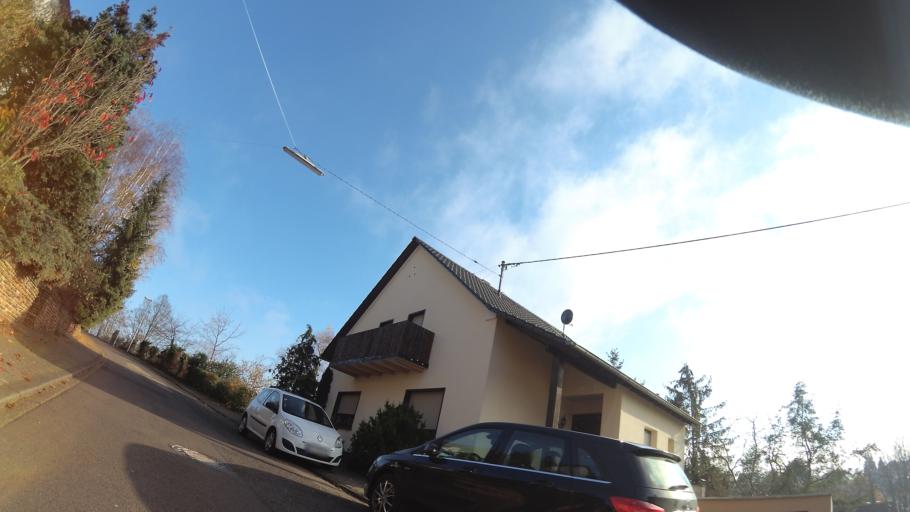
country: DE
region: Saarland
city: Ensdorf
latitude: 49.3098
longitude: 6.7813
